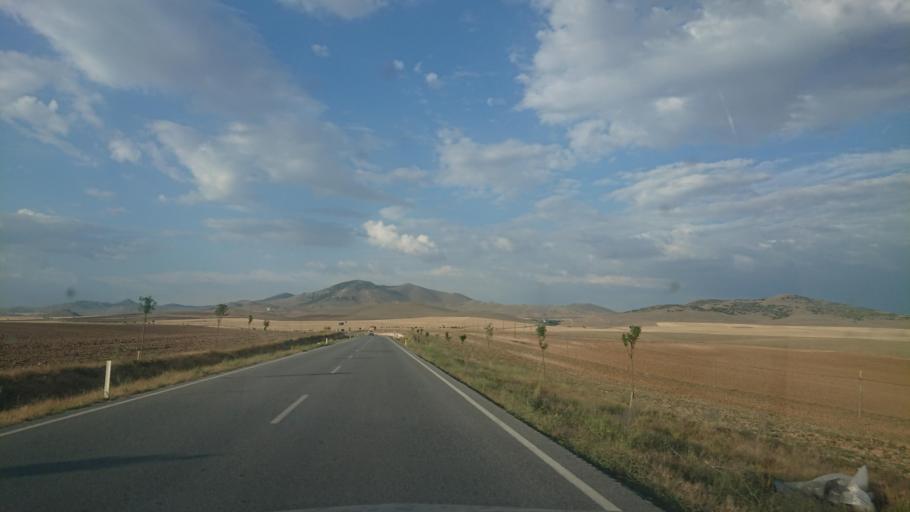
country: TR
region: Aksaray
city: Aksaray
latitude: 38.5085
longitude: 34.0848
